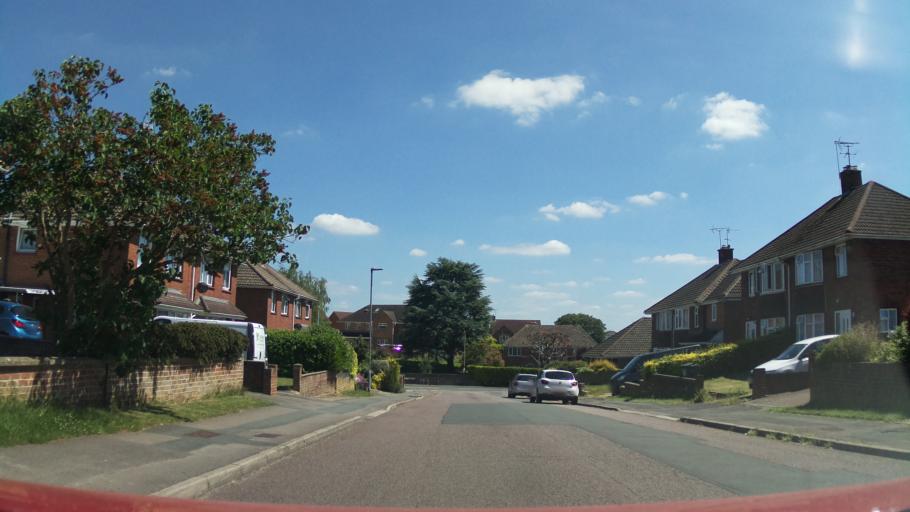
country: GB
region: England
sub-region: Wiltshire
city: Royal Wootton Bassett
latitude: 51.5443
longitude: -1.8921
